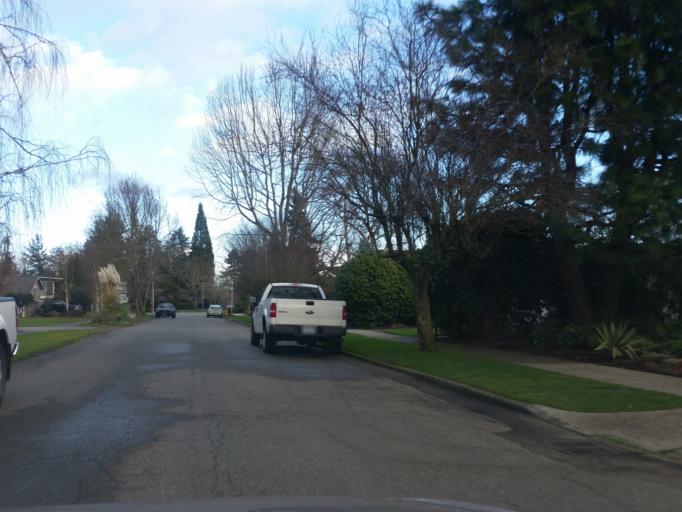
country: US
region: Washington
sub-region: King County
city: Lake Forest Park
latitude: 47.7488
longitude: -122.2820
